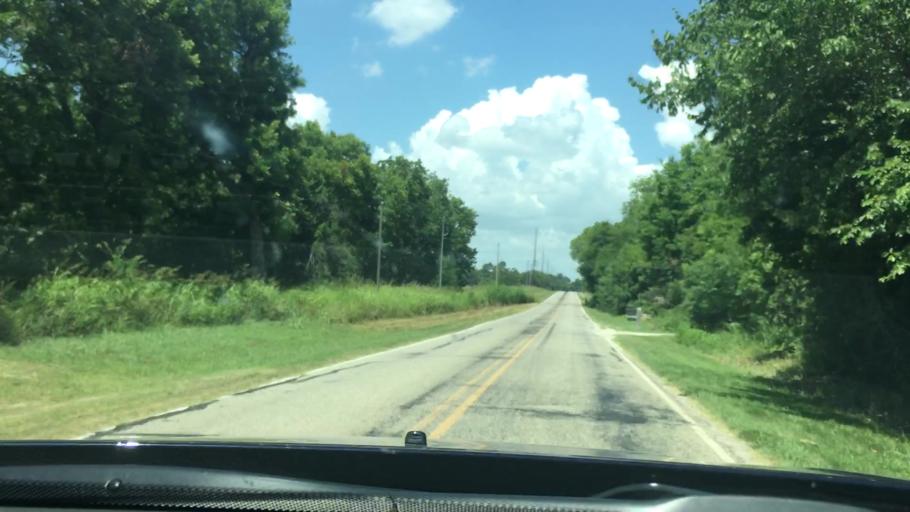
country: US
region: Oklahoma
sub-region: Pontotoc County
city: Ada
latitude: 34.6946
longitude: -96.5672
